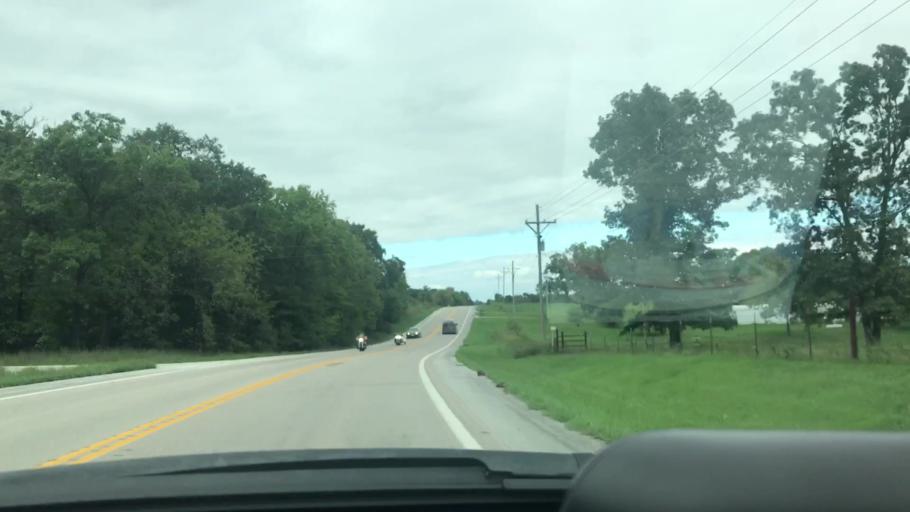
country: US
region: Missouri
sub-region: Hickory County
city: Hermitage
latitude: 37.8713
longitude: -93.1807
